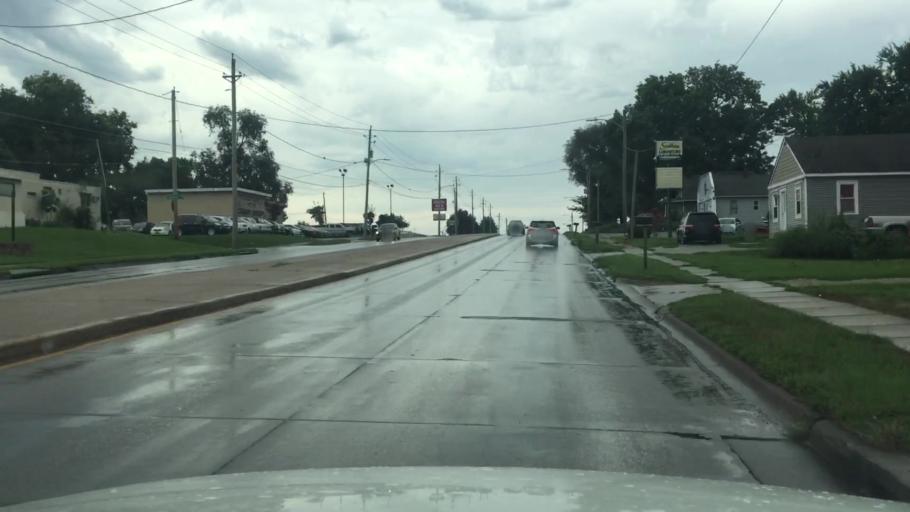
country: US
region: Iowa
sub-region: Polk County
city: Des Moines
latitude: 41.5594
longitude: -93.5970
